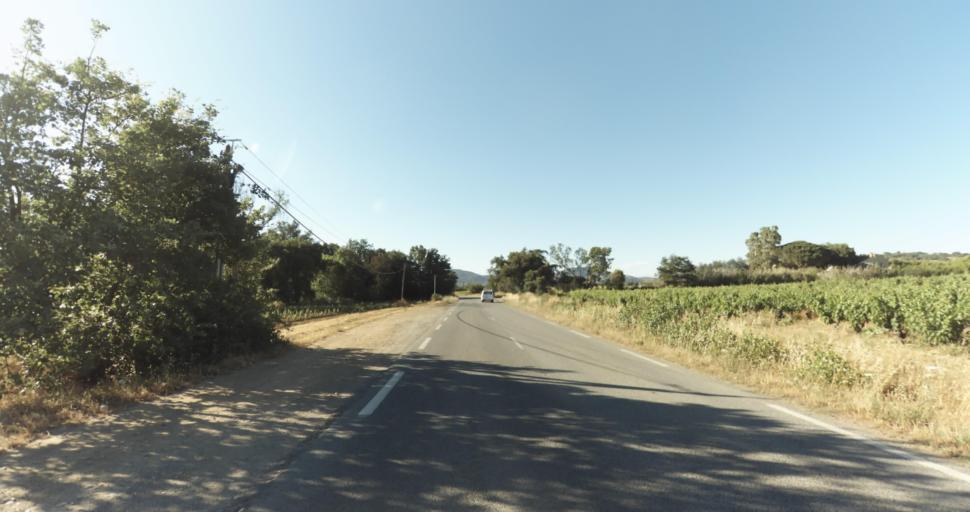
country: FR
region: Provence-Alpes-Cote d'Azur
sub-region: Departement du Var
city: Gassin
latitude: 43.2468
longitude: 6.5942
